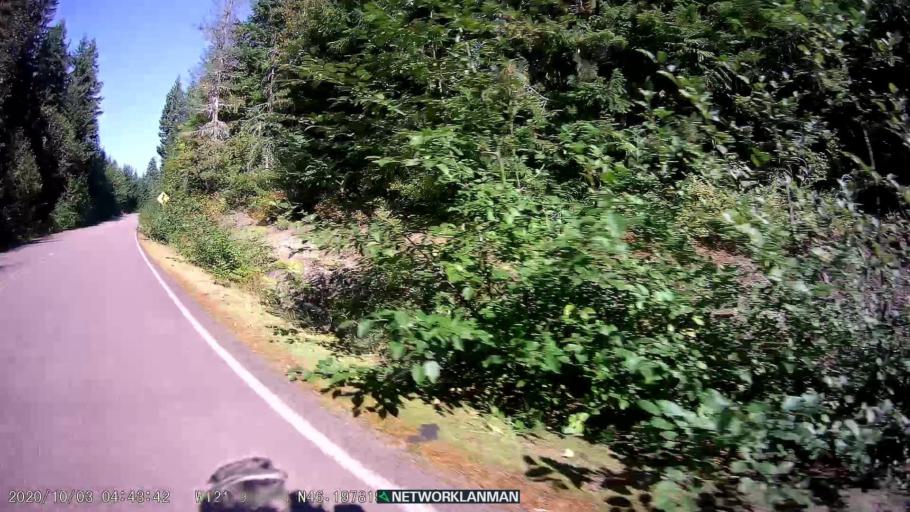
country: US
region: Washington
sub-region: Lewis County
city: Morton
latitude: 46.1979
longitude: -121.9952
